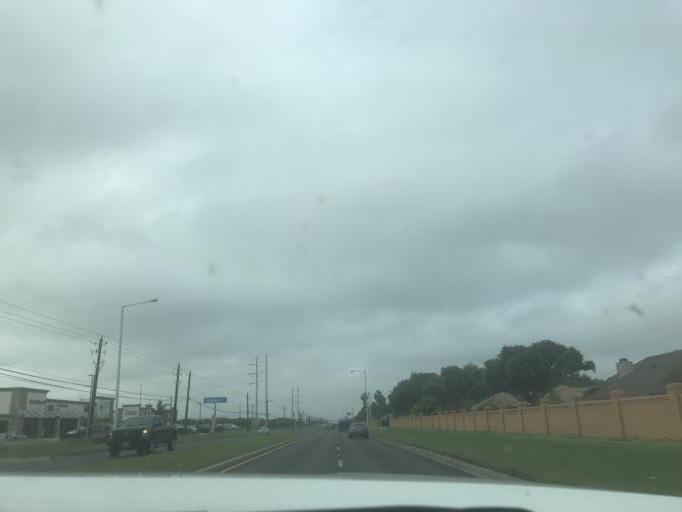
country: US
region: Texas
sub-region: Nueces County
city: Corpus Christi
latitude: 27.6802
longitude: -97.3730
